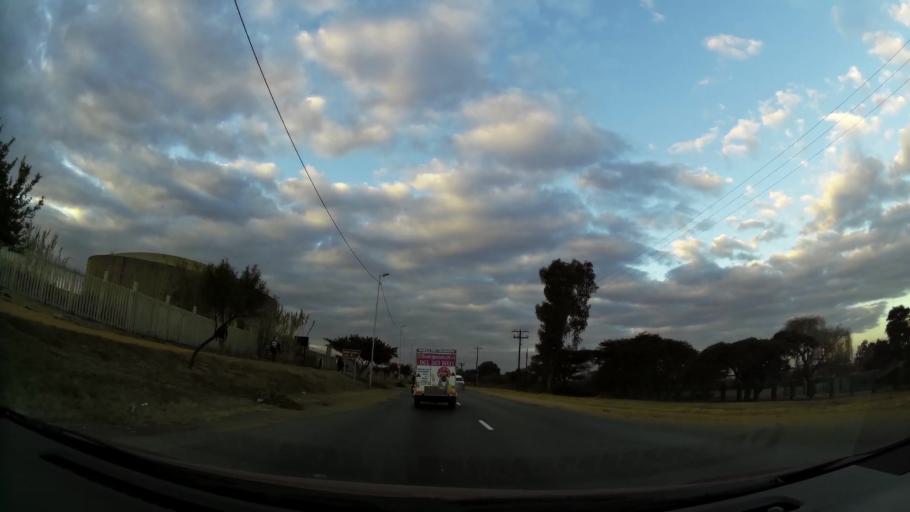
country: ZA
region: Gauteng
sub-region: City of Johannesburg Metropolitan Municipality
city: Midrand
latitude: -25.9940
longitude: 28.1468
